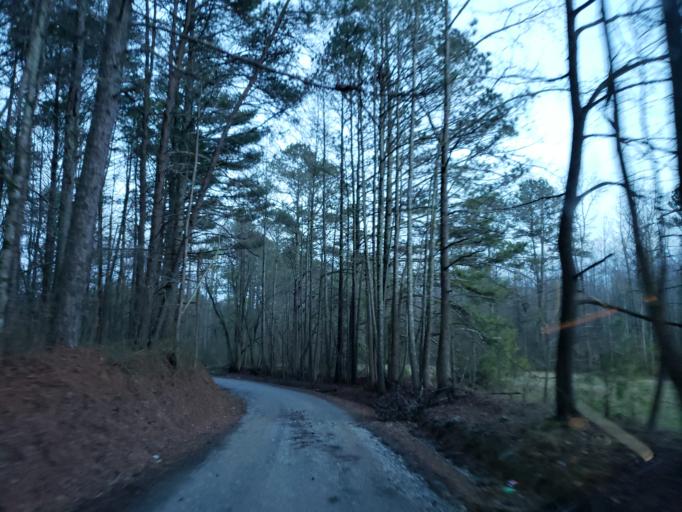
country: US
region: Georgia
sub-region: Cherokee County
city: Ball Ground
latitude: 34.2886
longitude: -84.3031
